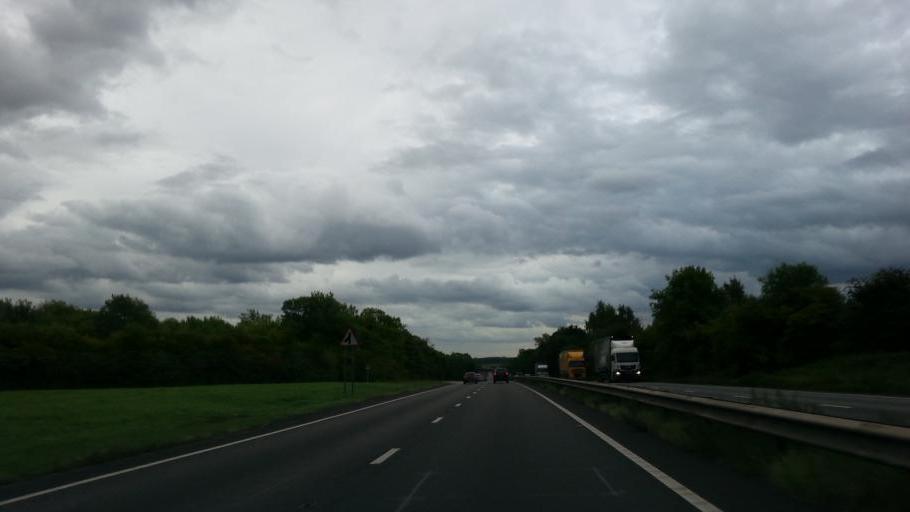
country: GB
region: England
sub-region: Nottinghamshire
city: Tuxford
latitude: 53.2307
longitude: -0.8949
